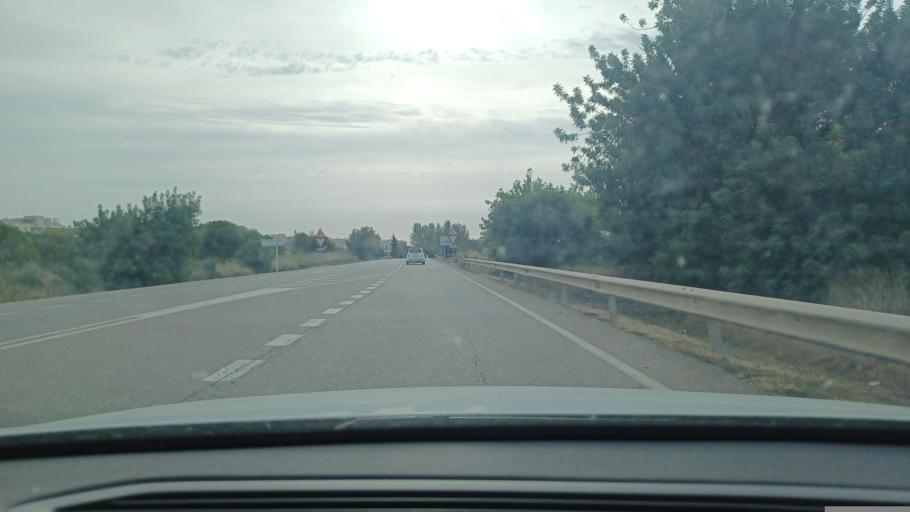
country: ES
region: Catalonia
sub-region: Provincia de Tarragona
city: Cambrils
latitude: 41.0728
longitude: 1.0465
